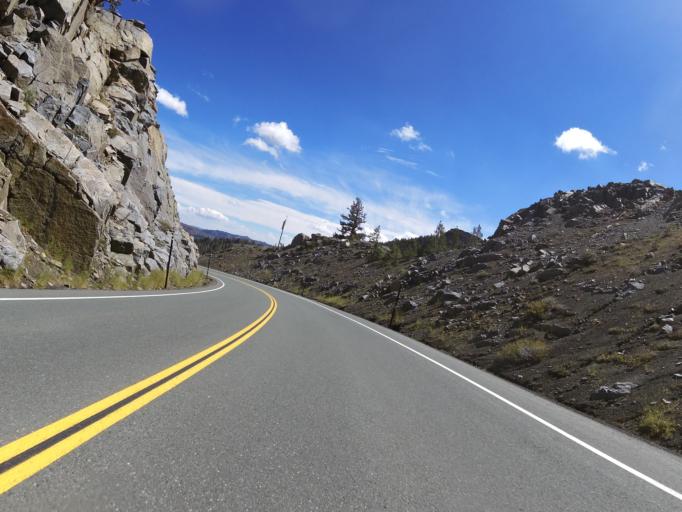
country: US
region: California
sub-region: El Dorado County
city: South Lake Tahoe
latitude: 38.6938
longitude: -119.9880
